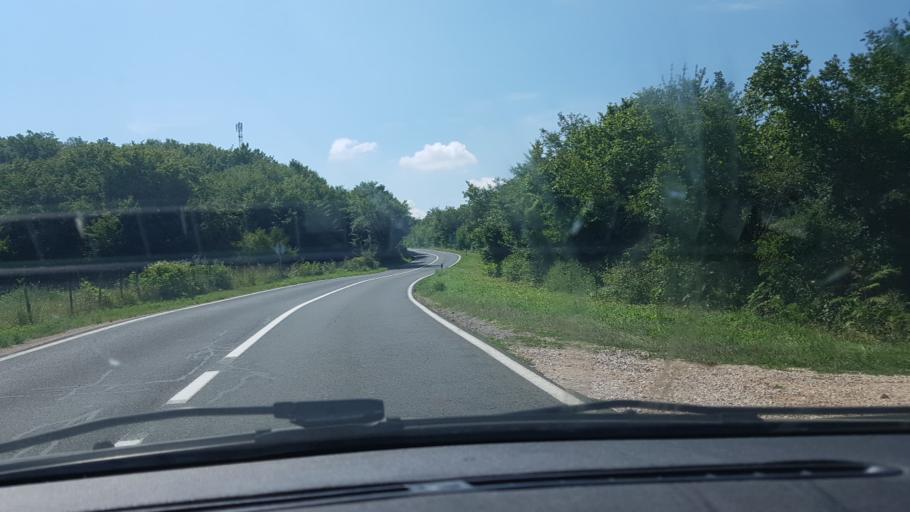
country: HR
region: Licko-Senjska
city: Otocac
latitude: 44.8812
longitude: 15.2007
